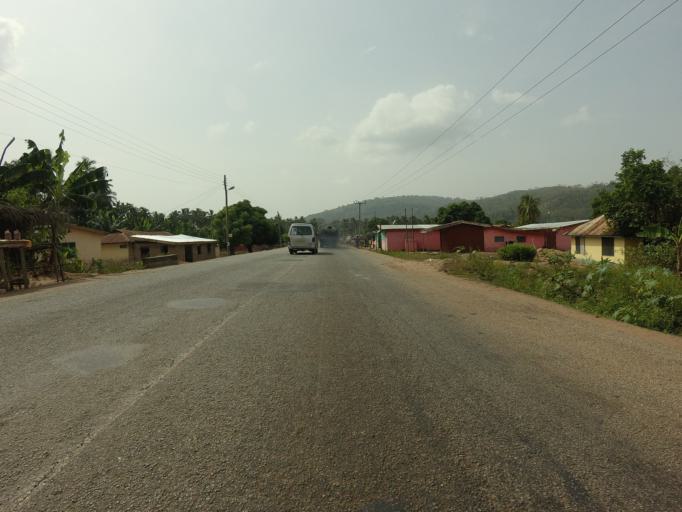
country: GH
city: Akropong
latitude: 6.2945
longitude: 0.1335
